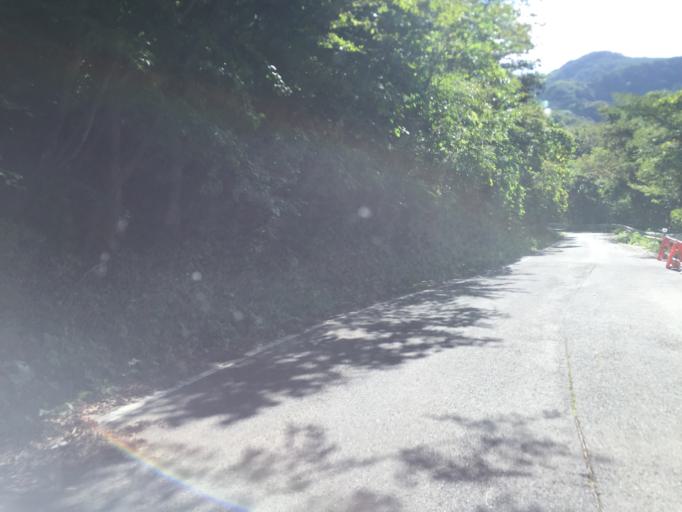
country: JP
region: Fukushima
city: Yanagawamachi-saiwaicho
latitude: 37.8334
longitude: 140.7001
